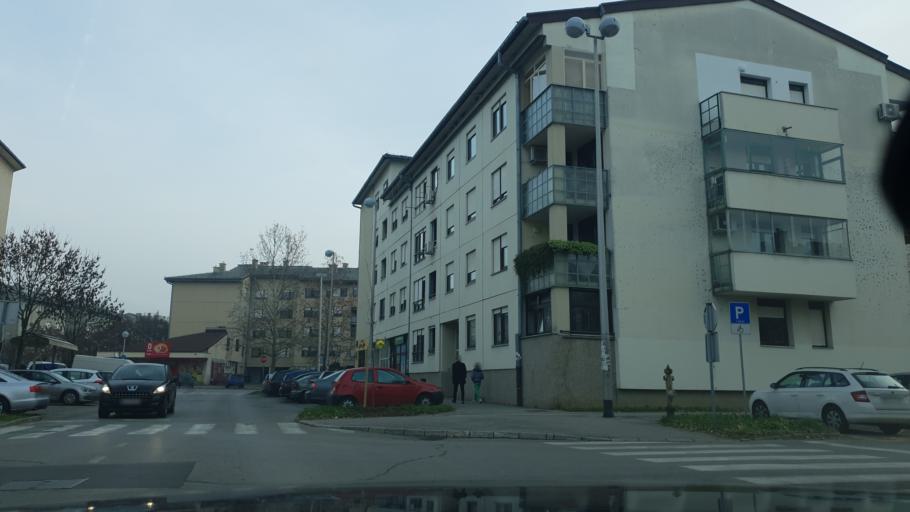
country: HR
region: Grad Zagreb
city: Jankomir
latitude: 45.7933
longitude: 15.9146
